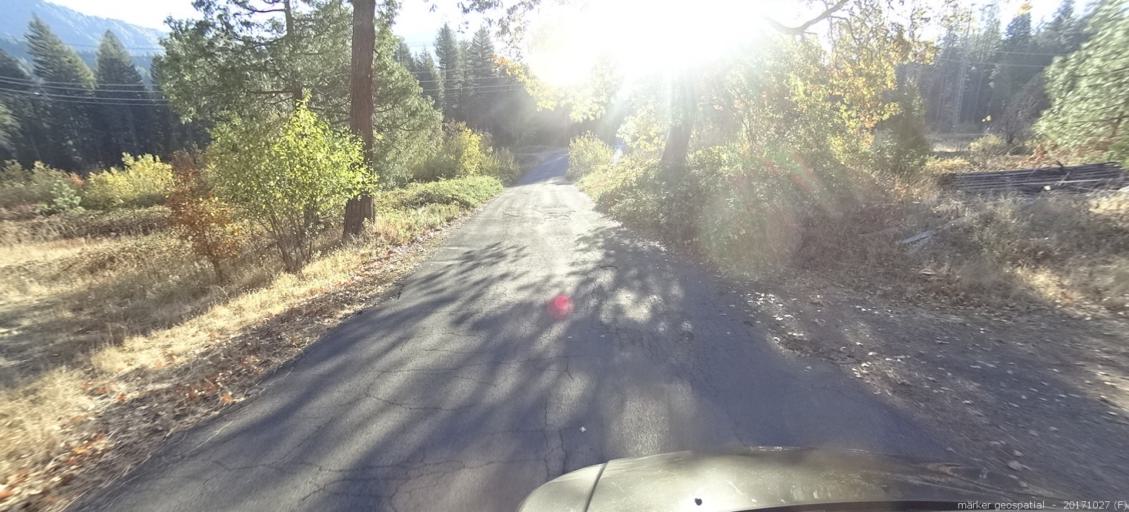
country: US
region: California
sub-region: Shasta County
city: Burney
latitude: 41.0077
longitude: -121.8952
